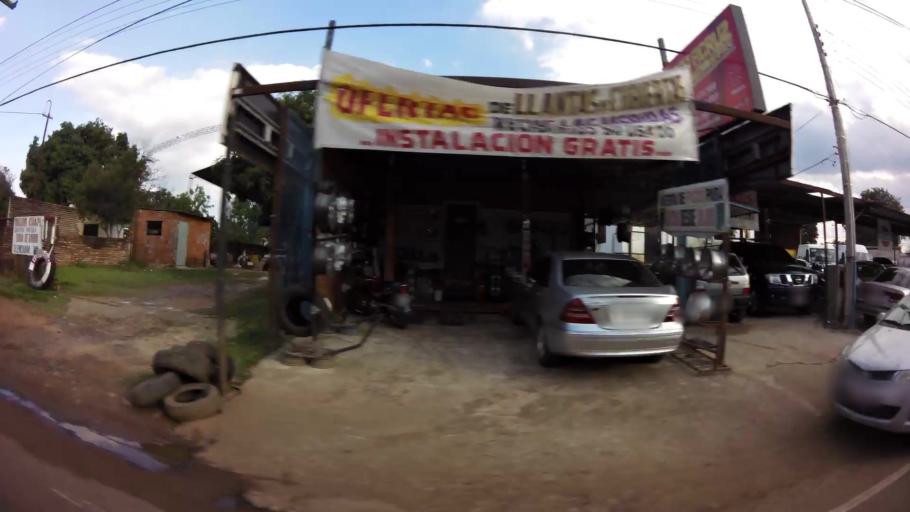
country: PY
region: Central
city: Fernando de la Mora
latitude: -25.3542
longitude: -57.5402
